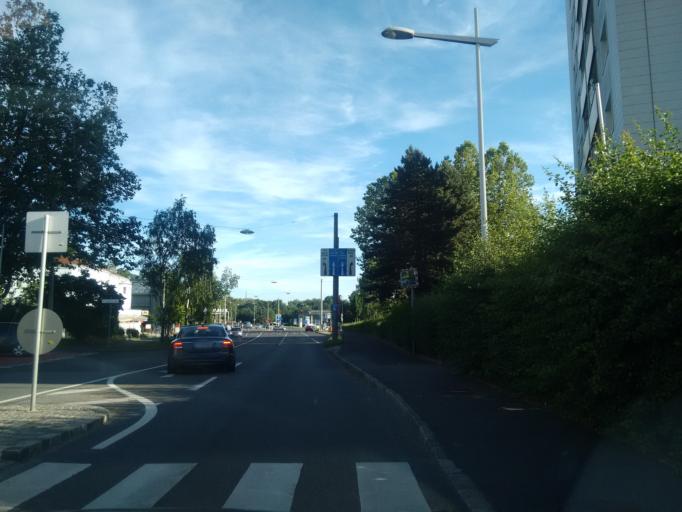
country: AT
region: Upper Austria
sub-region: Linz Stadt
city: Linz
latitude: 48.3311
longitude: 14.3176
